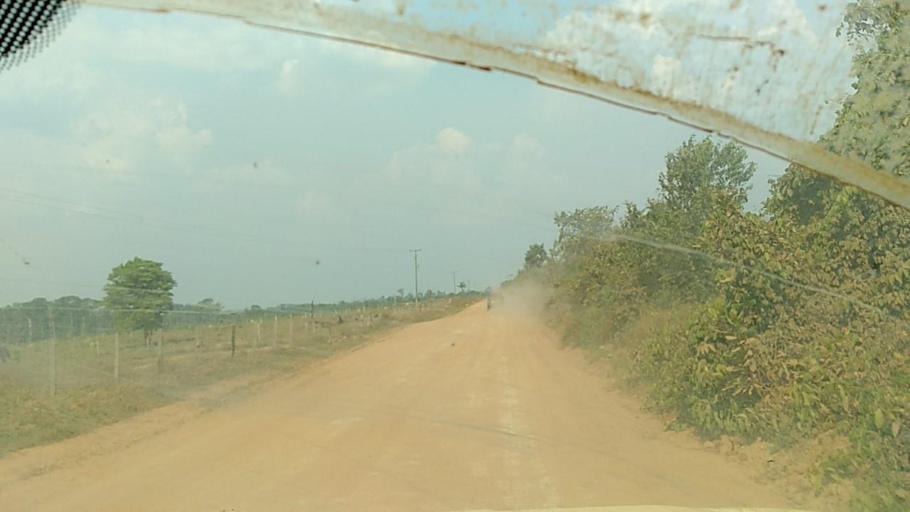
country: BR
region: Rondonia
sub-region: Porto Velho
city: Porto Velho
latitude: -8.6832
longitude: -63.2198
